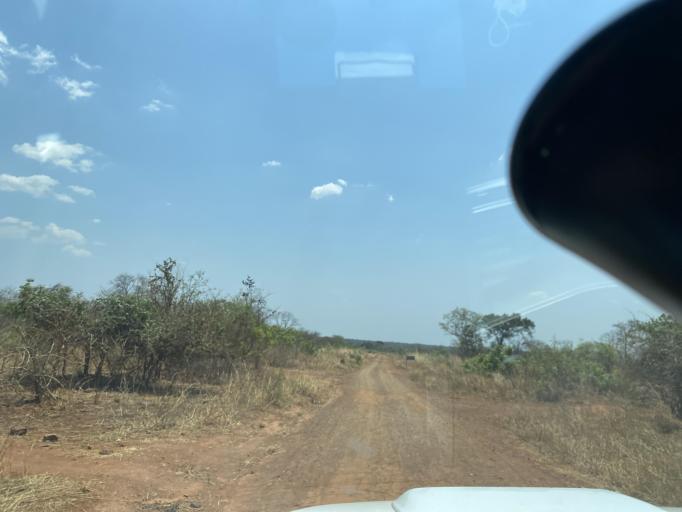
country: ZM
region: Lusaka
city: Lusaka
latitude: -15.5060
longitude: 28.0162
